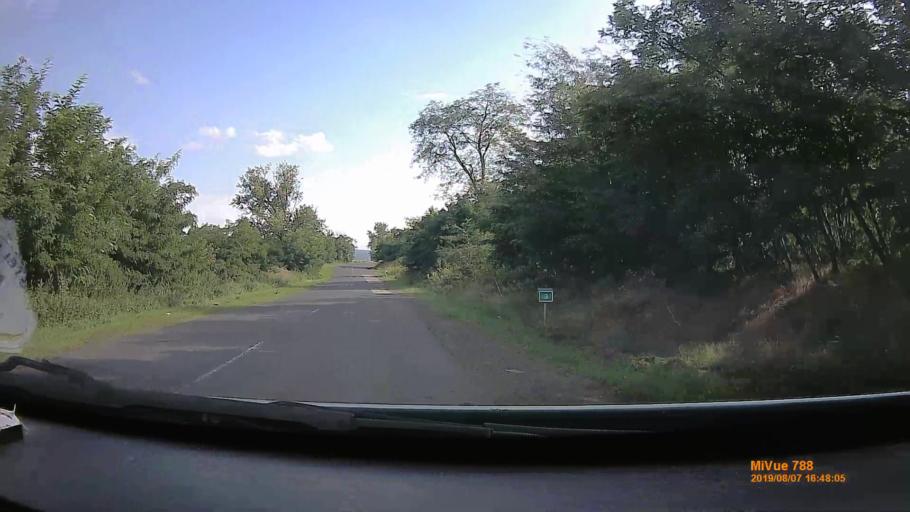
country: HU
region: Borsod-Abauj-Zemplen
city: Abaujszanto
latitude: 48.3351
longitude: 21.2049
